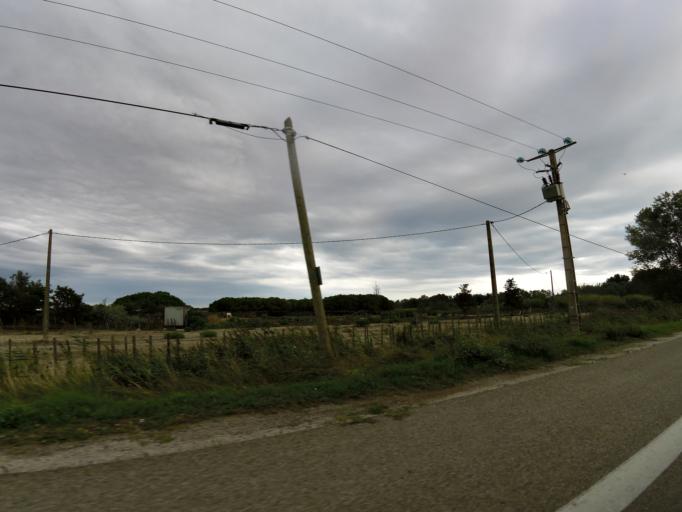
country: FR
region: Languedoc-Roussillon
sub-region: Departement du Gard
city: Le Grau-du-Roi
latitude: 43.5609
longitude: 4.1566
